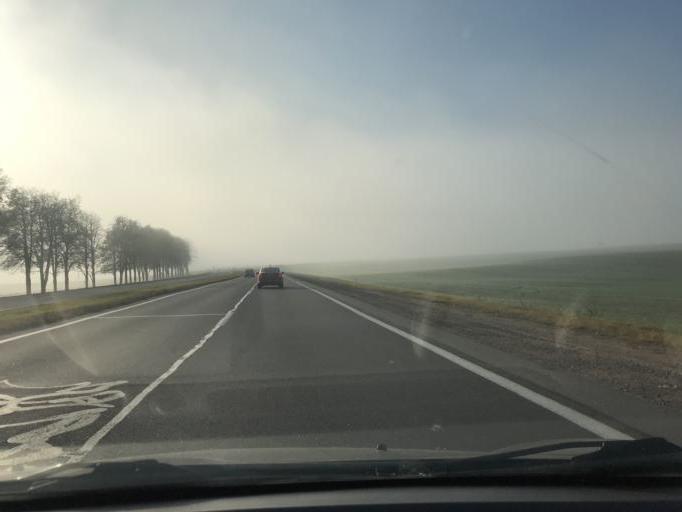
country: BY
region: Minsk
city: Luhavaya Slabada
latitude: 53.7545
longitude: 27.8313
